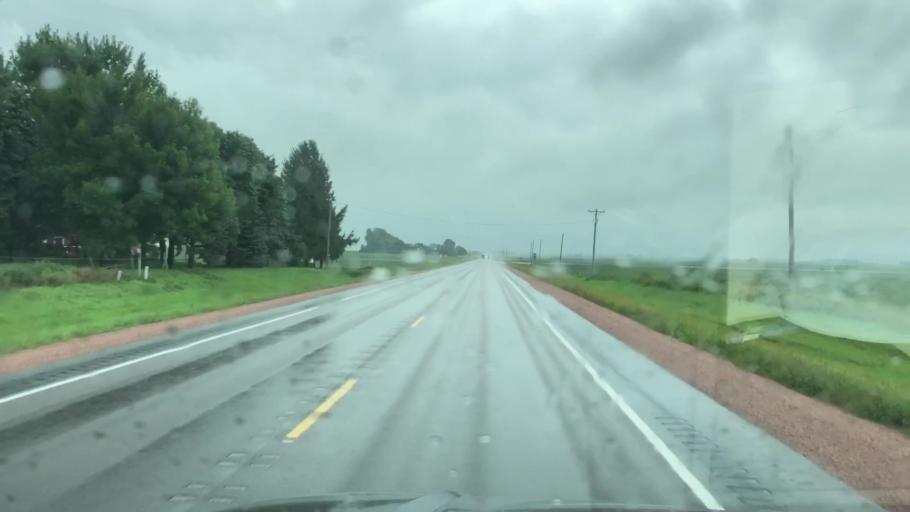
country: US
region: Iowa
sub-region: O'Brien County
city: Sheldon
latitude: 43.1862
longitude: -95.7575
